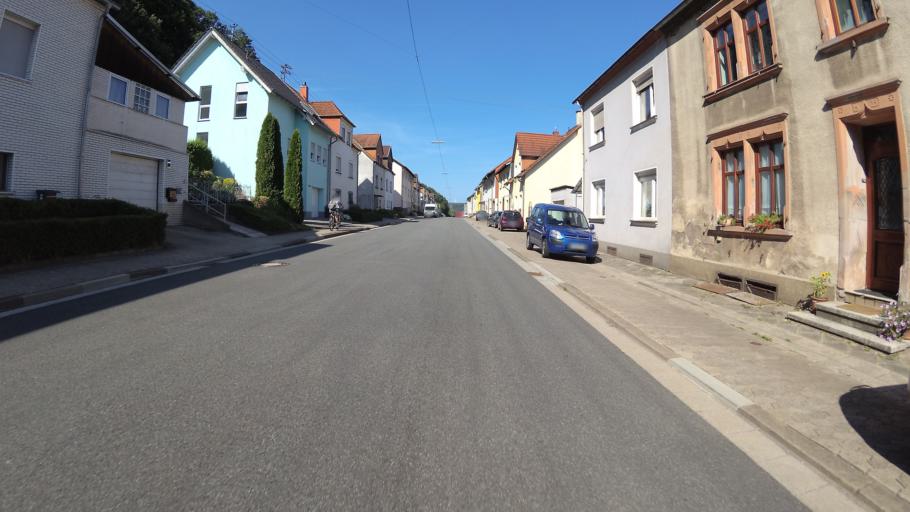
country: DE
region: Saarland
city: Eppelborn
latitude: 49.3954
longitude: 6.9610
